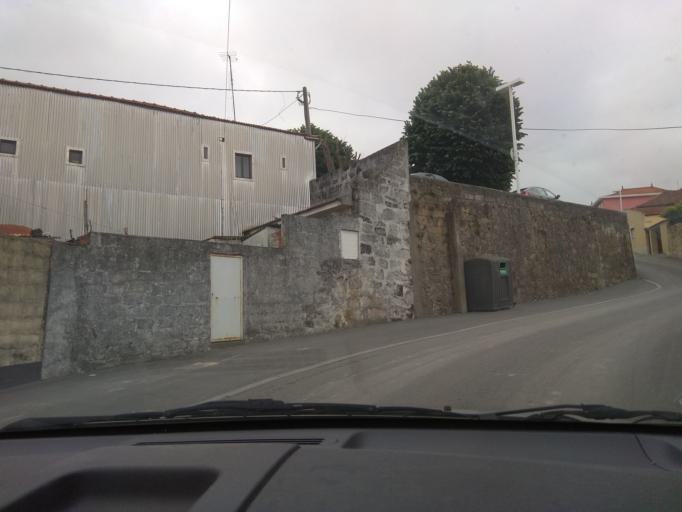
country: PT
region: Porto
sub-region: Matosinhos
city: Guifoes
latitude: 41.2013
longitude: -8.6659
